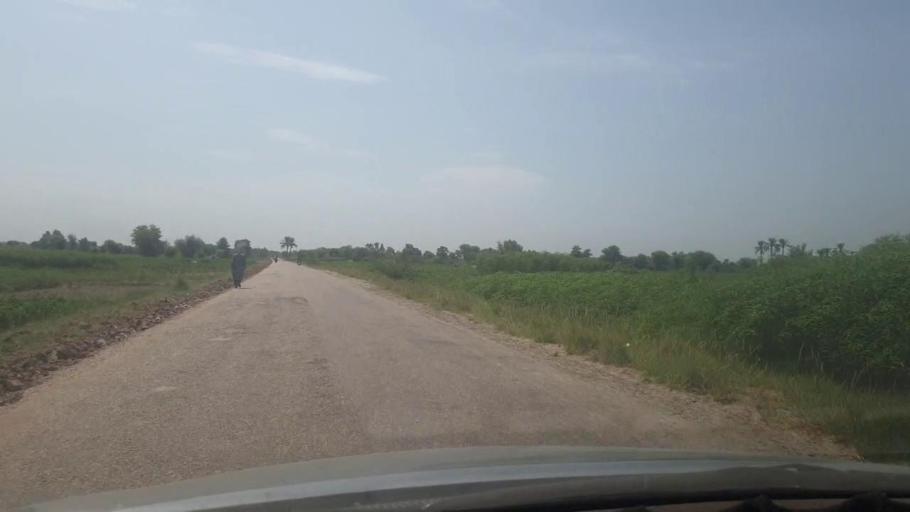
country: PK
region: Sindh
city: Bozdar
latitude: 27.2165
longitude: 68.5707
